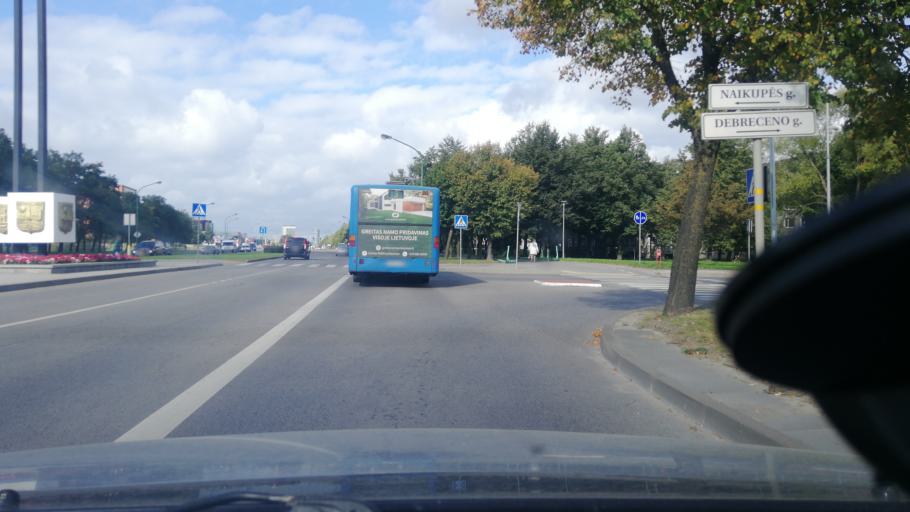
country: LT
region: Klaipedos apskritis
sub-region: Klaipeda
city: Klaipeda
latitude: 55.6804
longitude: 21.1651
